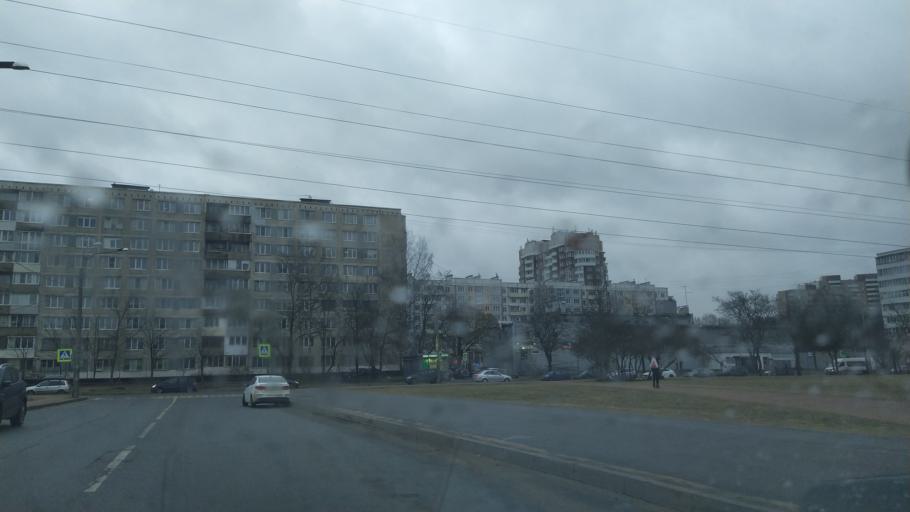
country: RU
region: Leningrad
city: Akademicheskoe
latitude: 60.0231
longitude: 30.3917
